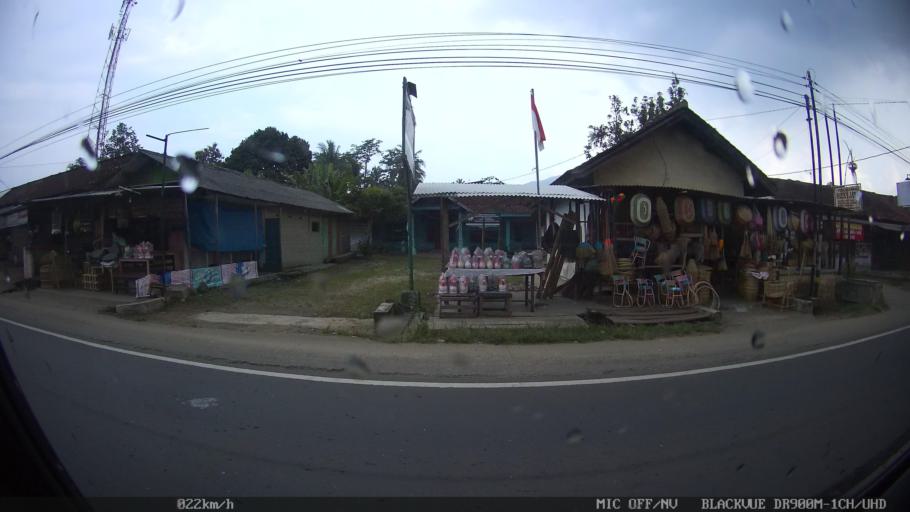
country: ID
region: Lampung
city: Gedongtataan
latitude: -5.3774
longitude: 105.1271
